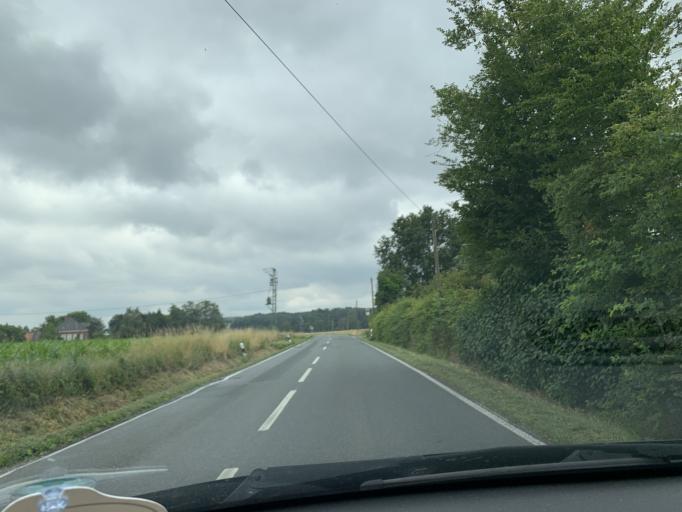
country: DE
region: North Rhine-Westphalia
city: Oelde
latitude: 51.8258
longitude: 8.0888
